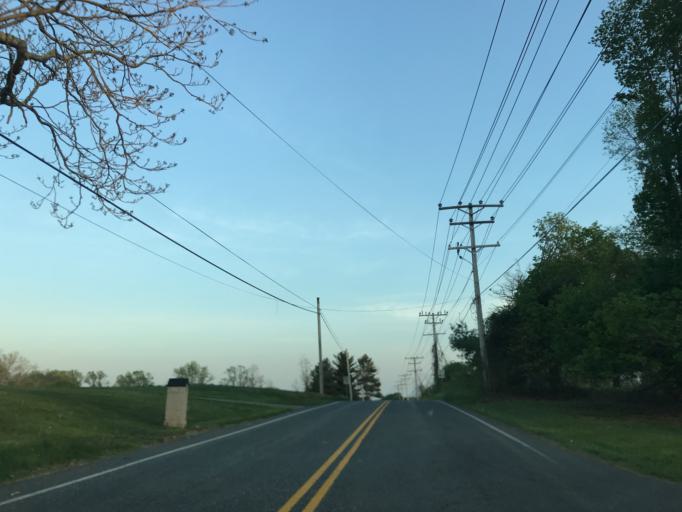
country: US
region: Maryland
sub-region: Harford County
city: Jarrettsville
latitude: 39.5864
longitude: -76.4295
